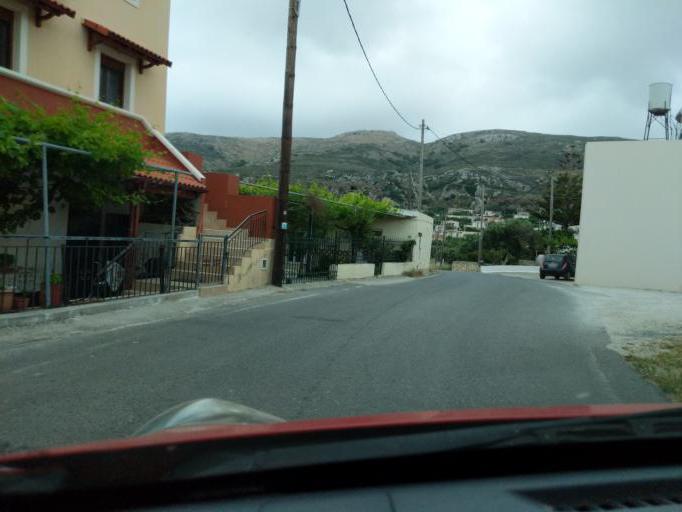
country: GR
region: Crete
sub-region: Nomos Chanias
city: Platanos
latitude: 35.4743
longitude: 23.5998
